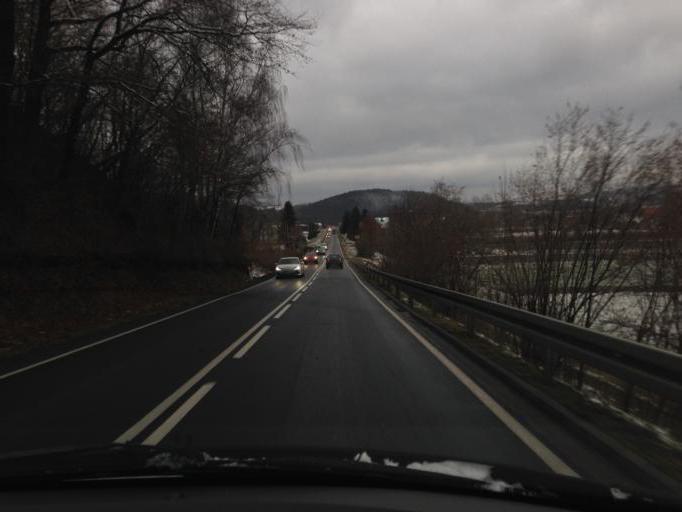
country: PL
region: Lesser Poland Voivodeship
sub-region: Powiat tarnowski
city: Zakliczyn
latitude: 49.8670
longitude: 20.8006
